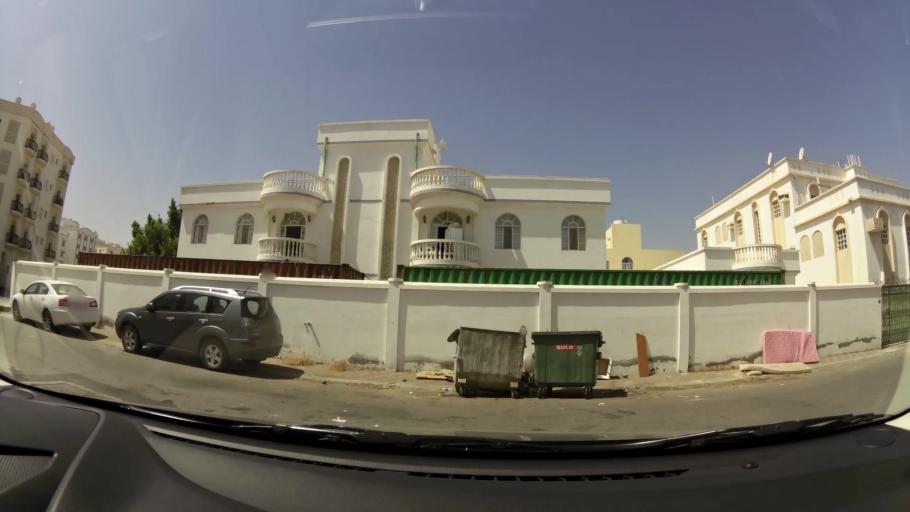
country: OM
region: Muhafazat Masqat
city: Bawshar
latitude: 23.5886
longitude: 58.4017
